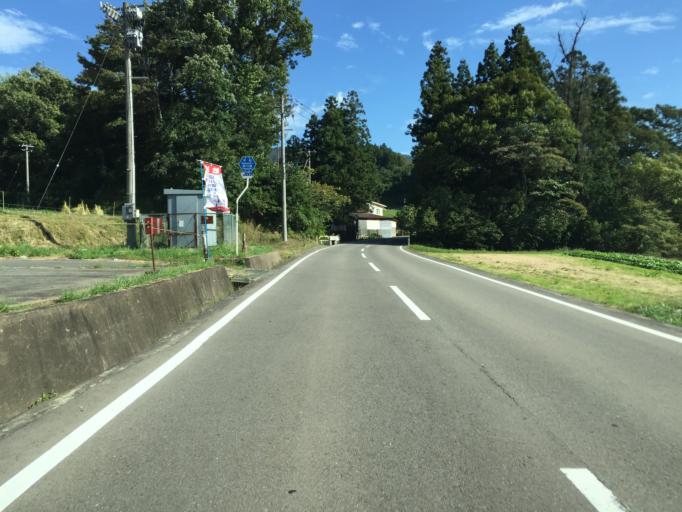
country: JP
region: Fukushima
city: Yanagawamachi-saiwaicho
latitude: 37.8511
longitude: 140.6507
